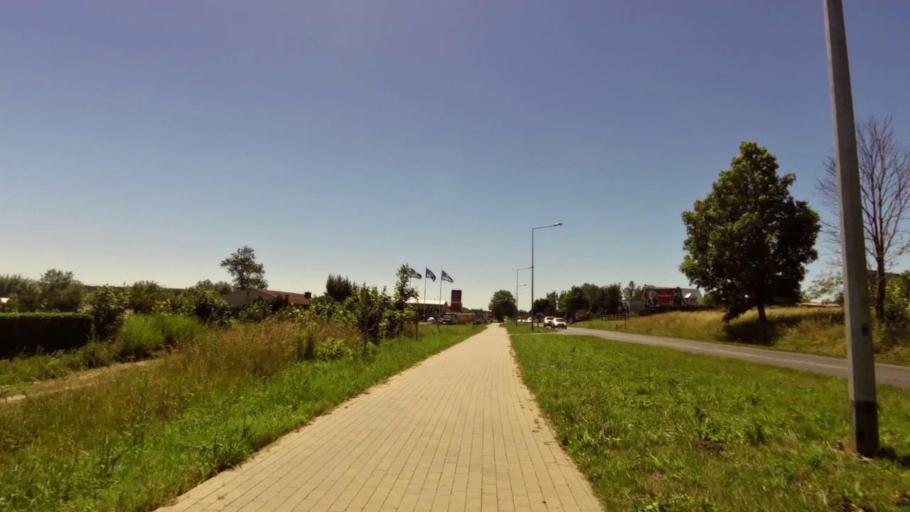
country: PL
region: West Pomeranian Voivodeship
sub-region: Powiat kolobrzeski
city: Kolobrzeg
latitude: 54.1404
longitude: 15.5596
